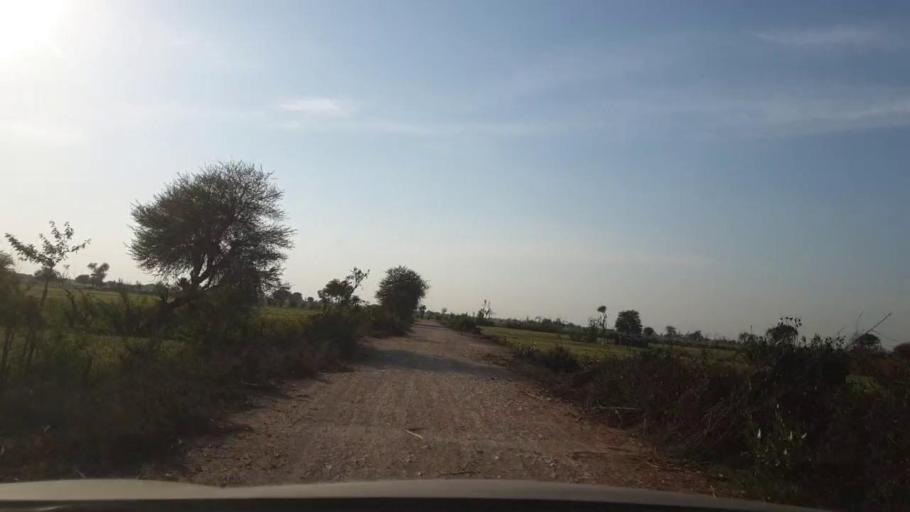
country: PK
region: Sindh
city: Tando Adam
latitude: 25.6937
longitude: 68.7040
